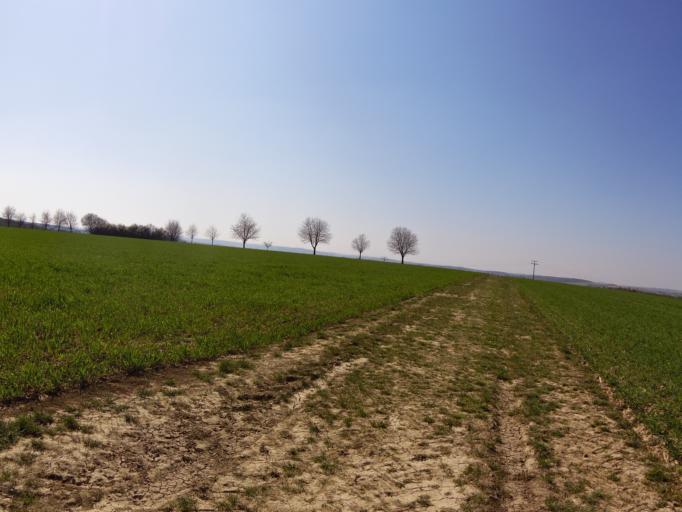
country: DE
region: Bavaria
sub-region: Regierungsbezirk Unterfranken
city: Kurnach
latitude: 49.8367
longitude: 10.0427
